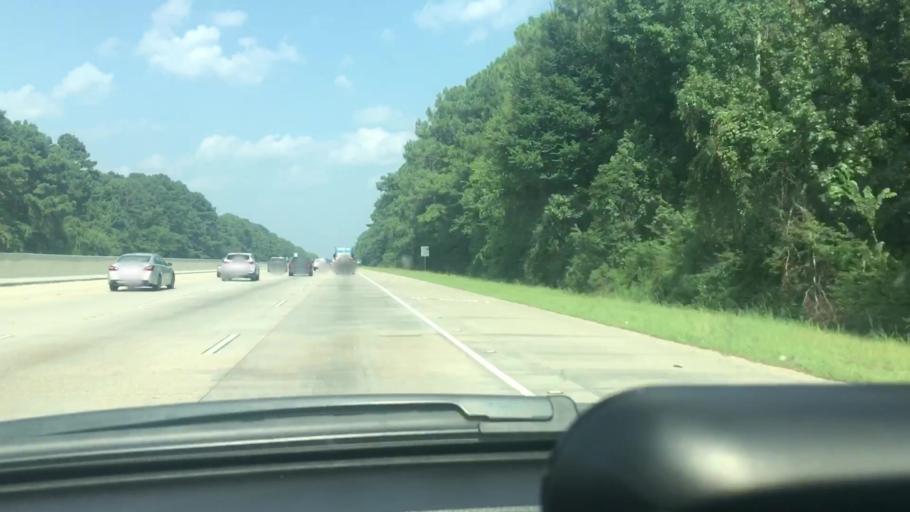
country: US
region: Louisiana
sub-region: Livingston Parish
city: Denham Springs
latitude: 30.4575
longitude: -90.9460
